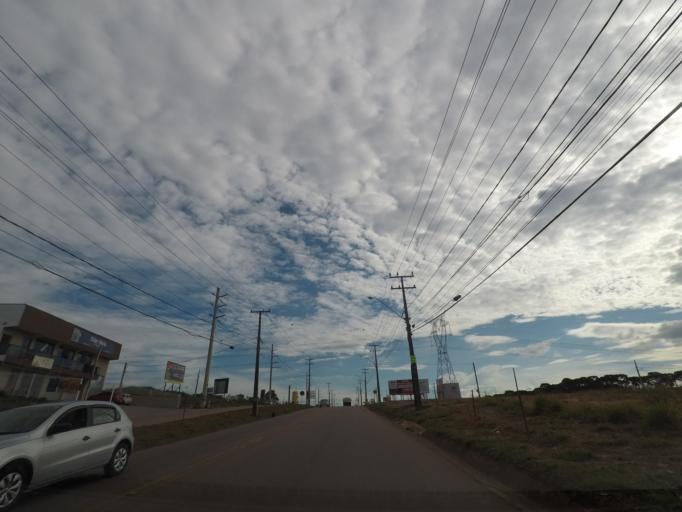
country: BR
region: Parana
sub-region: Araucaria
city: Araucaria
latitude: -25.6352
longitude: -49.2946
